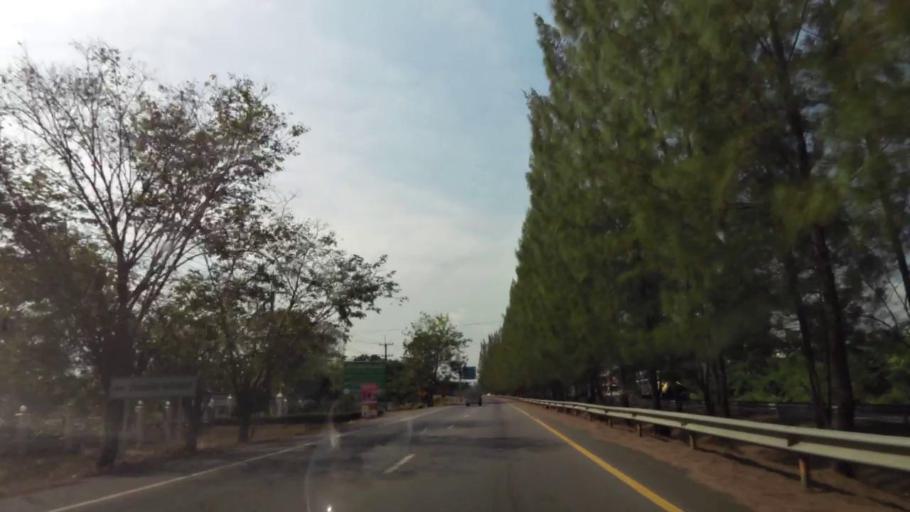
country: TH
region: Chanthaburi
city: Chanthaburi
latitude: 12.6666
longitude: 102.0973
